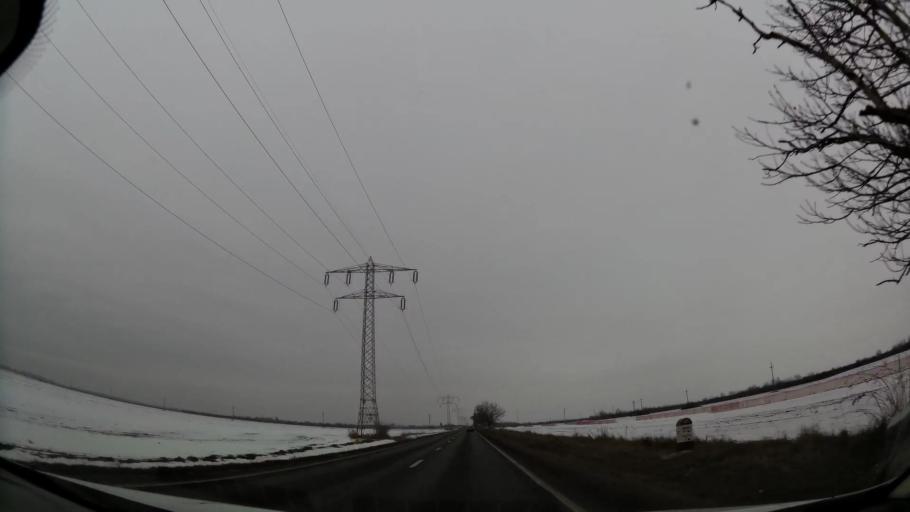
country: RO
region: Dambovita
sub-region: Comuna Salcioara
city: Salcioara
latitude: 44.7277
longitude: 25.6088
